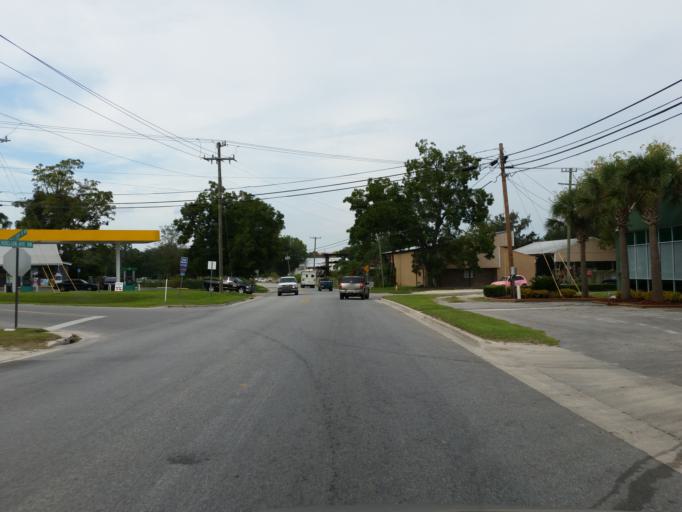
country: US
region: Florida
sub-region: Suwannee County
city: Live Oak
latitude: 30.3043
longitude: -82.9851
